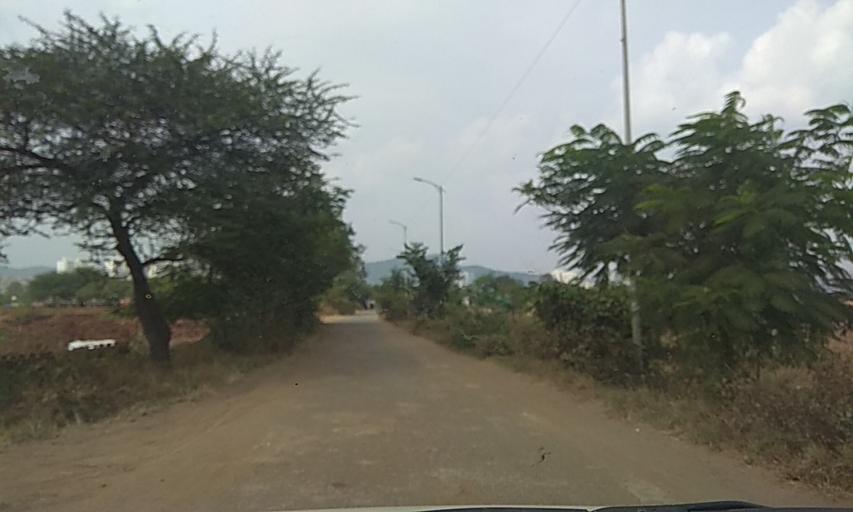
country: IN
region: Maharashtra
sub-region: Pune Division
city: Pimpri
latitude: 18.5797
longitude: 73.7079
